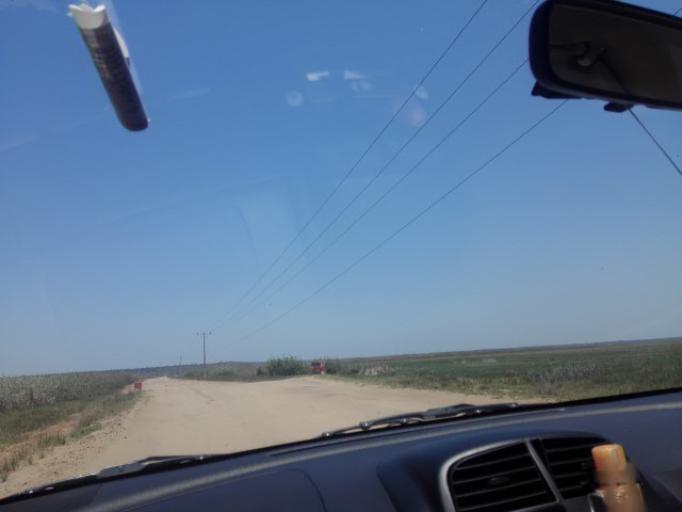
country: MZ
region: Maputo City
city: Maputo
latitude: -25.7313
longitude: 32.7175
